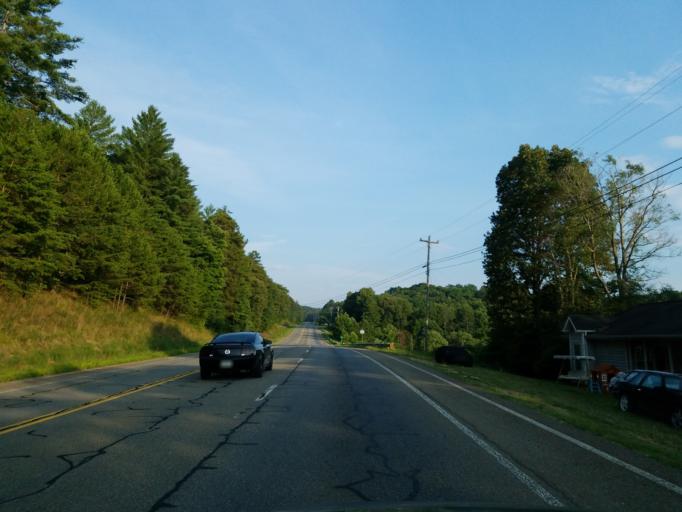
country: US
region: Georgia
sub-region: Gilmer County
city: Ellijay
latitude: 34.6684
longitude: -84.4539
